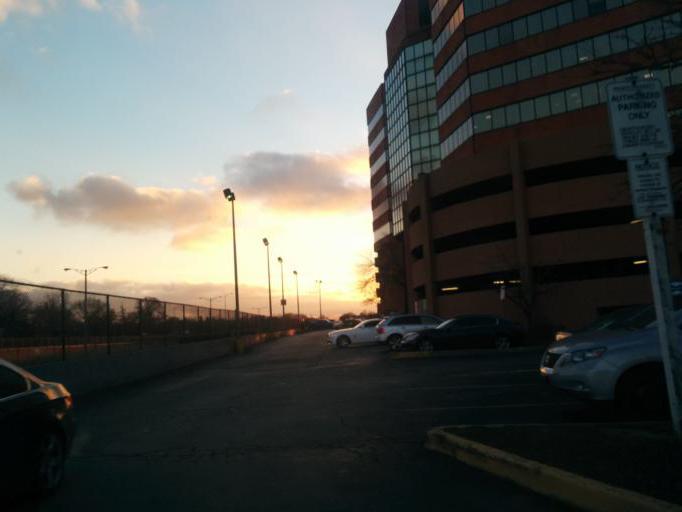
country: CA
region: Ontario
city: Etobicoke
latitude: 43.6084
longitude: -79.5565
